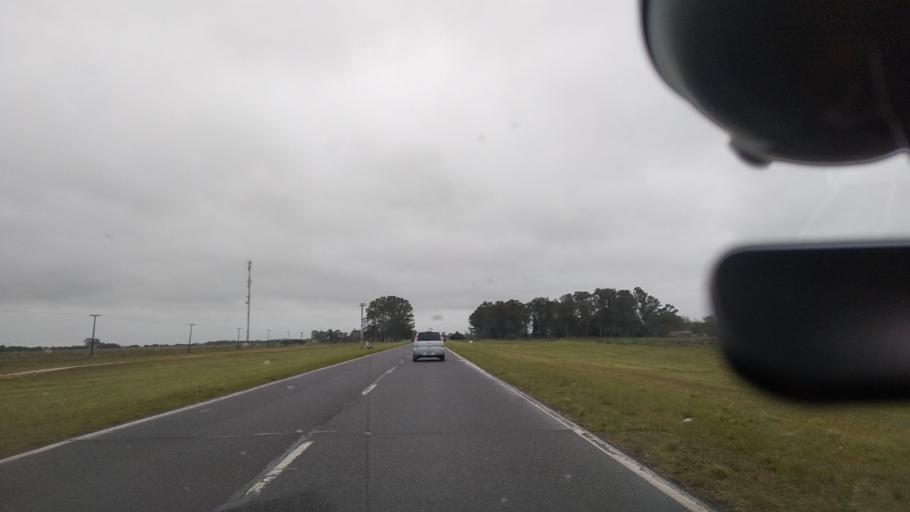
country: AR
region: Buenos Aires
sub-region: Partido de Castelli
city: Castelli
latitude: -35.9873
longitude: -57.4499
